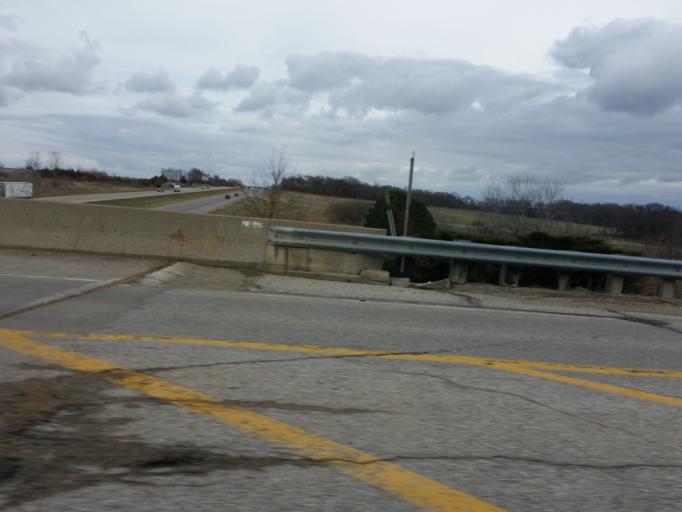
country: US
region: Iowa
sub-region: Black Hawk County
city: Elk Run Heights
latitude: 42.4492
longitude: -92.2196
